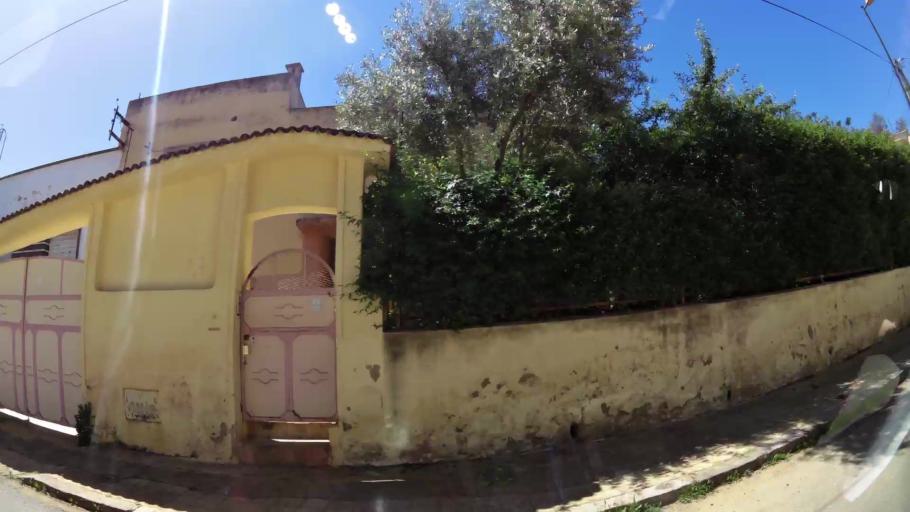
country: MA
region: Meknes-Tafilalet
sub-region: Meknes
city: Meknes
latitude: 33.9035
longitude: -5.5288
